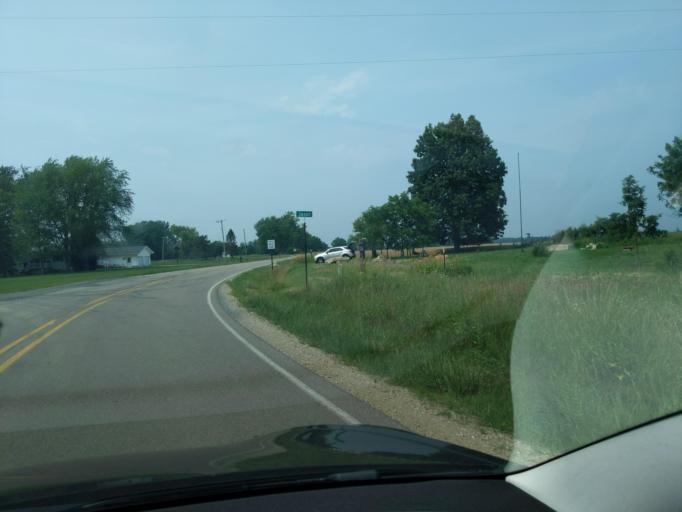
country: US
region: Michigan
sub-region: Clinton County
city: DeWitt
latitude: 42.9162
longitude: -84.5821
